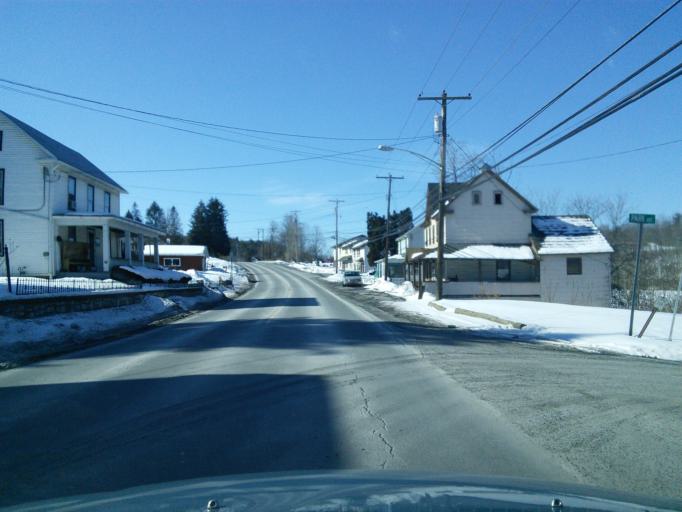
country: US
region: Pennsylvania
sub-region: Centre County
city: Bellefonte
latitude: 40.9042
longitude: -77.7929
